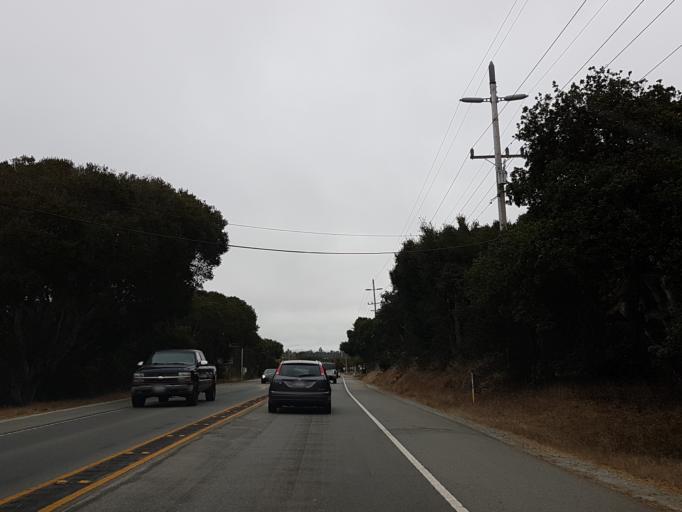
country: US
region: California
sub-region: Monterey County
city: Carmel Valley Village
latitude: 36.5705
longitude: -121.7645
